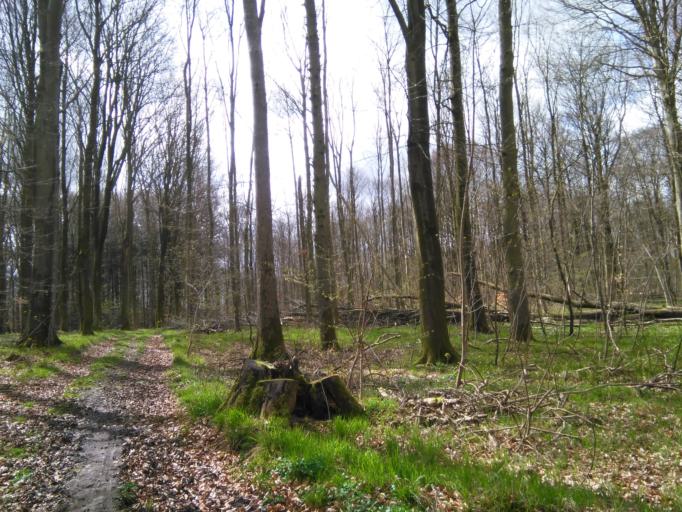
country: DK
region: Central Jutland
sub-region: Favrskov Kommune
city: Soften
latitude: 56.2265
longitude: 10.0749
